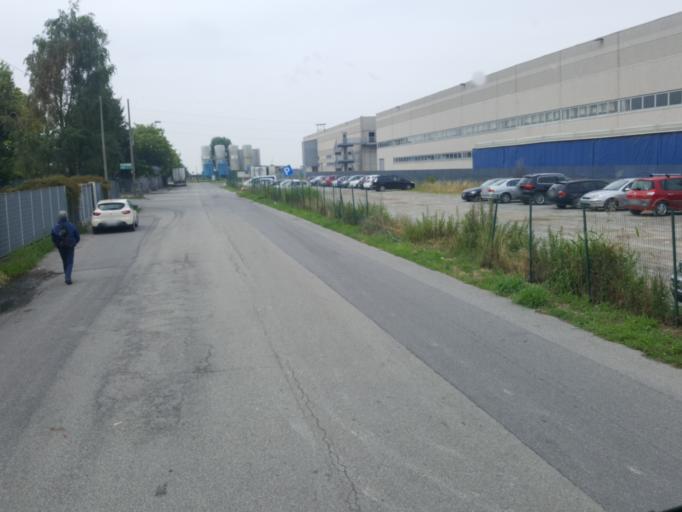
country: IT
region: Lombardy
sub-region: Provincia di Monza e Brianza
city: Cavenago di Brianza
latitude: 45.5805
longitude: 9.4087
